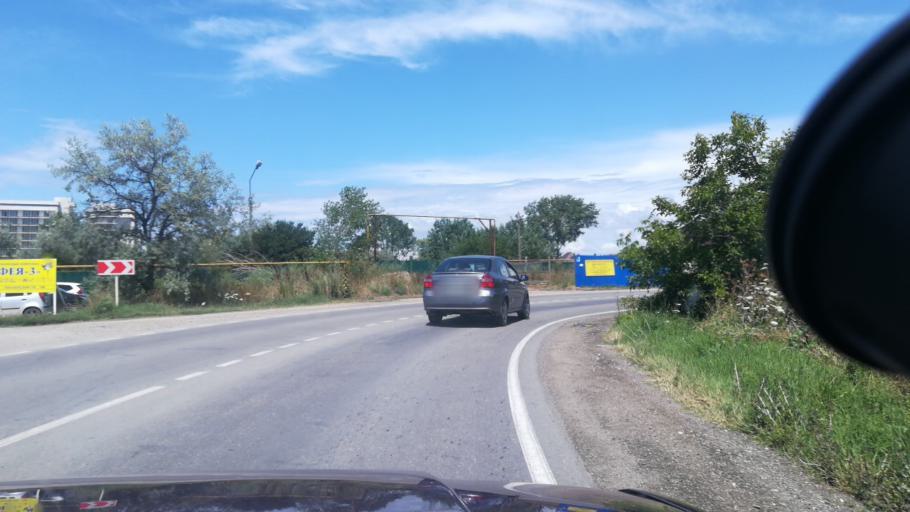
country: RU
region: Krasnodarskiy
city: Vityazevo
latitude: 44.9639
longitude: 37.2910
